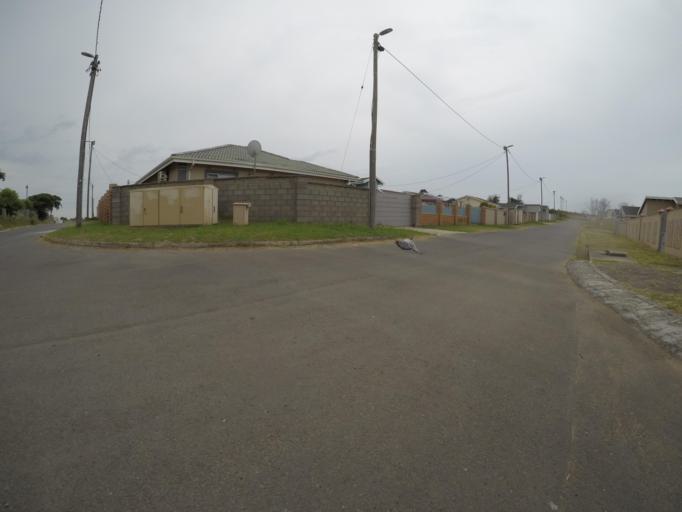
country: ZA
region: Eastern Cape
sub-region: Buffalo City Metropolitan Municipality
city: East London
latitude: -32.9984
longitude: 27.8471
